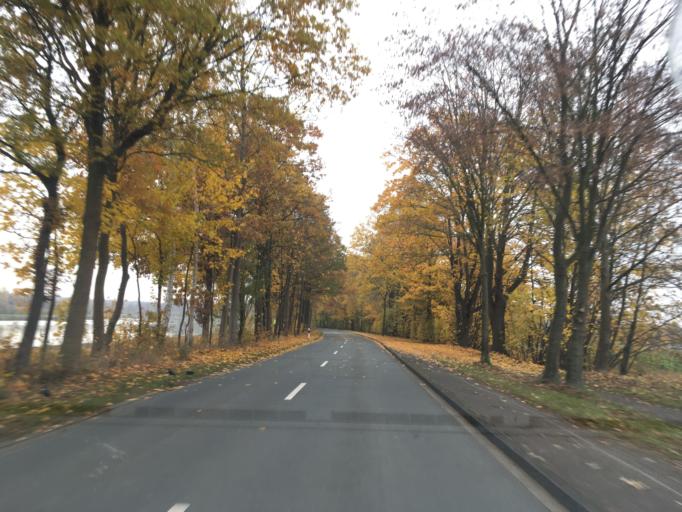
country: DE
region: North Rhine-Westphalia
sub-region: Regierungsbezirk Munster
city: Muenster
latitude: 51.8943
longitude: 7.6620
